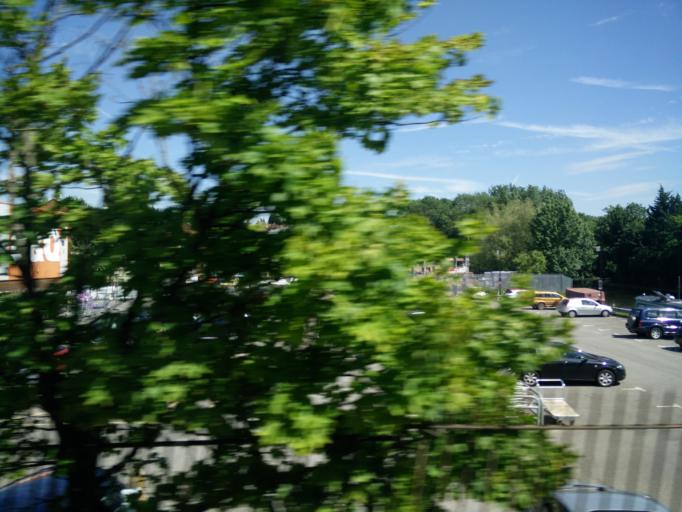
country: GB
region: England
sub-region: Hertfordshire
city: Hemel Hempstead
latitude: 51.7430
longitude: -0.4737
